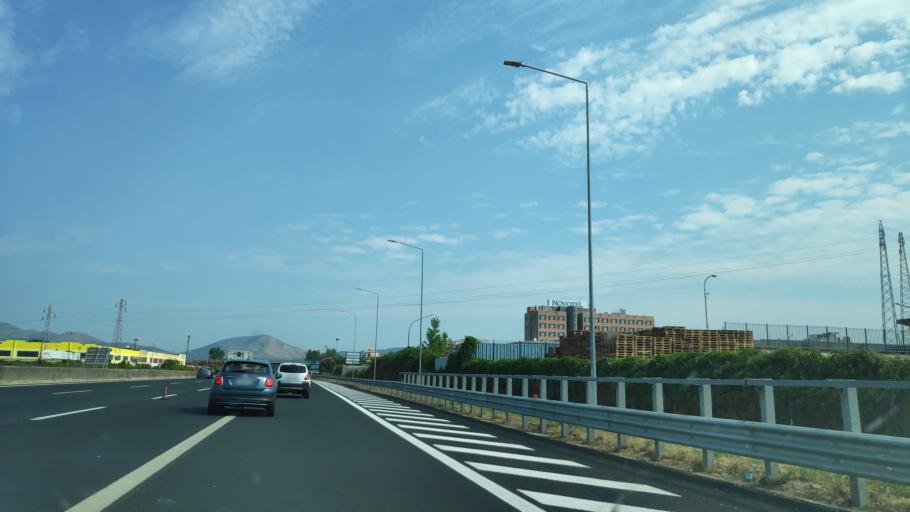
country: IT
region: Campania
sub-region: Provincia di Caserta
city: Capodrise
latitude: 41.0397
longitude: 14.3227
